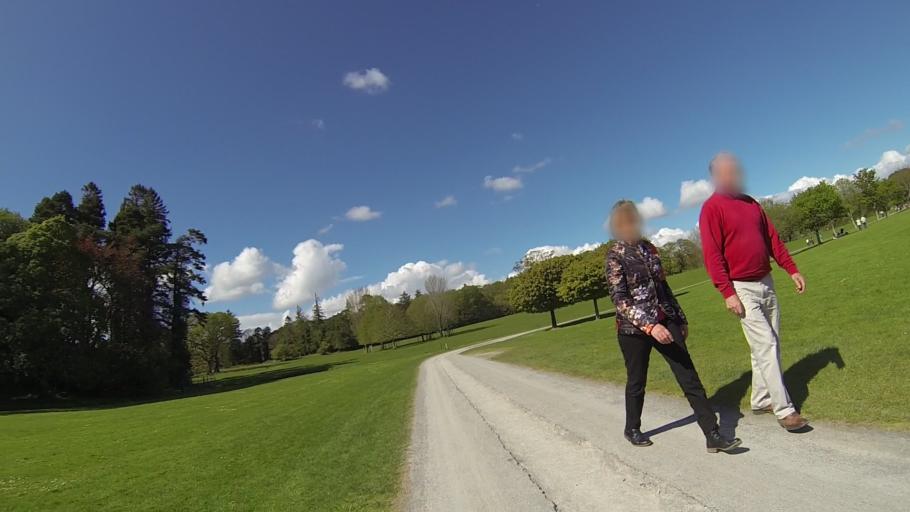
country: IE
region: Munster
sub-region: Ciarrai
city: Cill Airne
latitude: 52.0175
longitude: -9.5072
